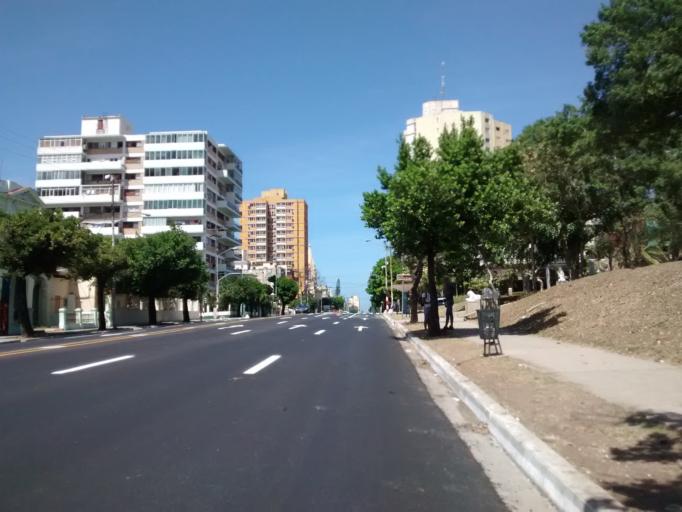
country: CU
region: La Habana
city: Havana
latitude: 23.1334
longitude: -82.3914
